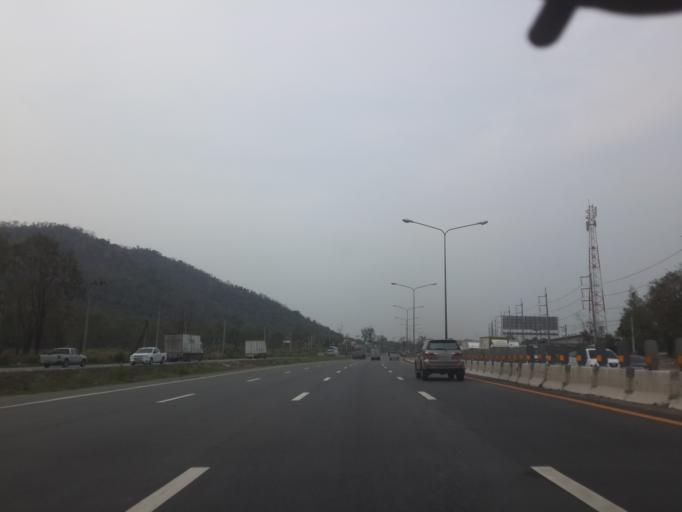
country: TH
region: Chon Buri
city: Si Racha
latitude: 13.2578
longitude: 100.9903
